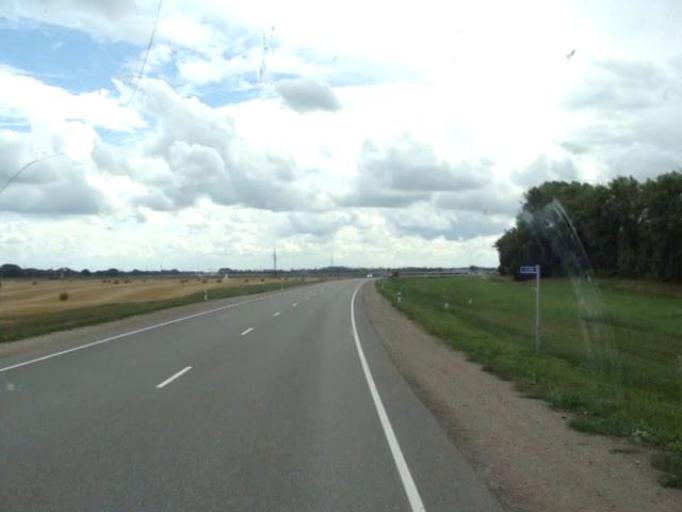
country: RU
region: Altai Krai
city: Shubenka
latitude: 52.6816
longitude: 85.0471
